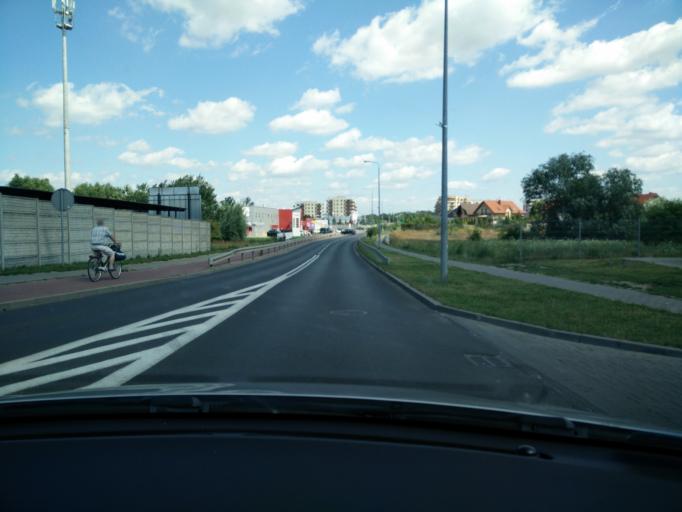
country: PL
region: Greater Poland Voivodeship
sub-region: Powiat sredzki
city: Sroda Wielkopolska
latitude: 52.2323
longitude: 17.2667
